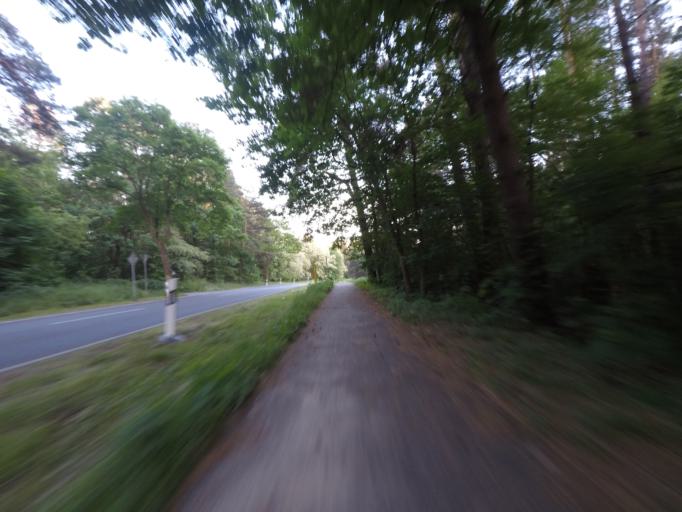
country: DE
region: Brandenburg
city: Marienwerder
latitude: 52.8597
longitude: 13.6493
